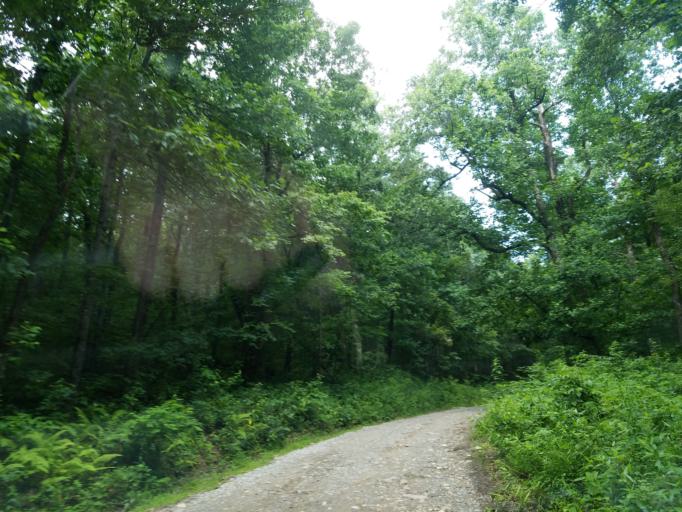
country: US
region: Georgia
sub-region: Lumpkin County
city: Dahlonega
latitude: 34.6360
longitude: -84.1727
